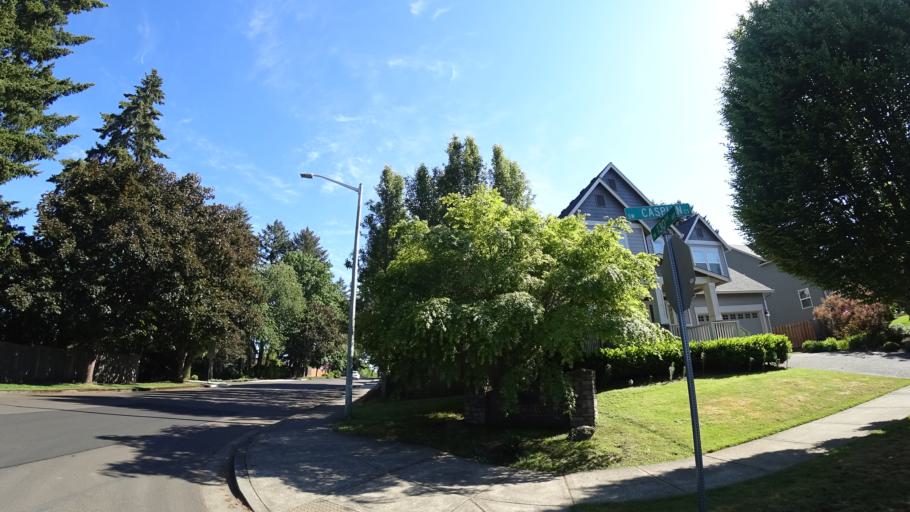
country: US
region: Oregon
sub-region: Washington County
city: Beaverton
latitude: 45.4521
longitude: -122.8107
